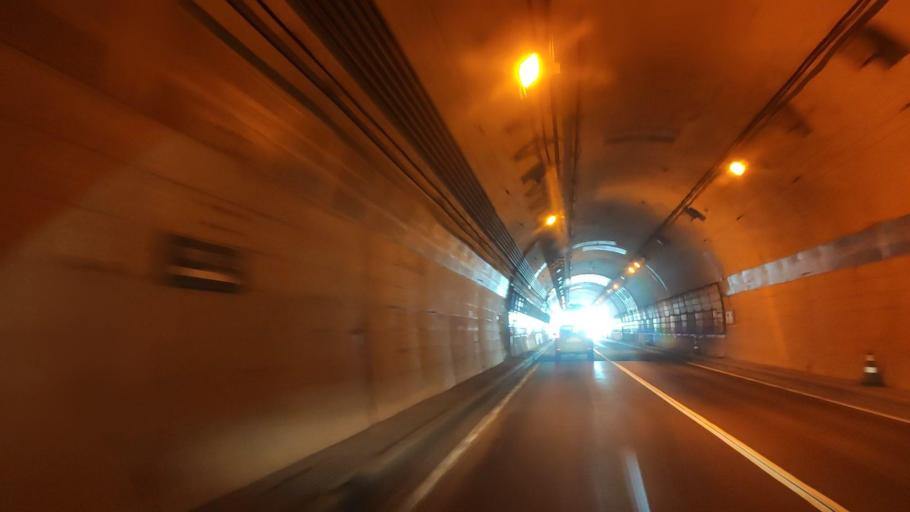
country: JP
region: Hokkaido
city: Rumoi
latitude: 43.7909
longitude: 141.3729
